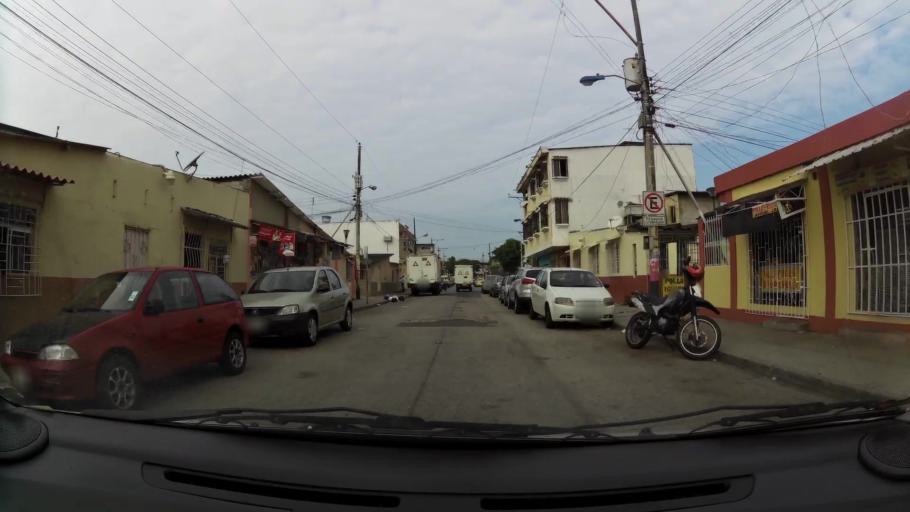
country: EC
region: Guayas
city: Guayaquil
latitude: -2.2536
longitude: -79.8875
